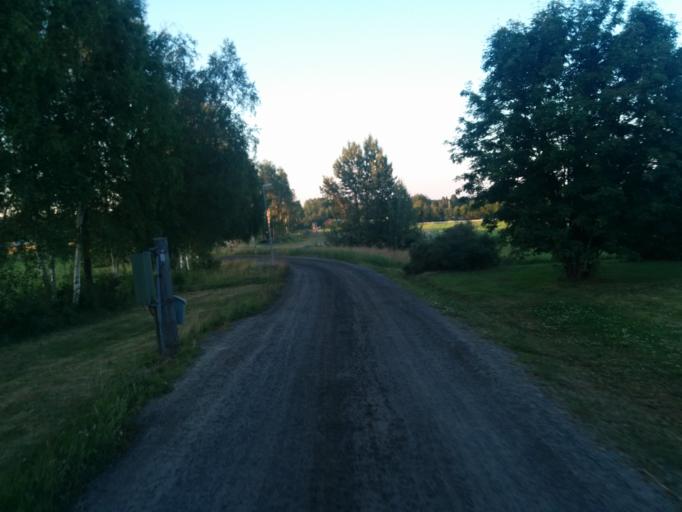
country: SE
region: Vaesterbotten
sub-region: Umea Kommun
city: Ersmark
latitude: 63.8523
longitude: 20.3785
